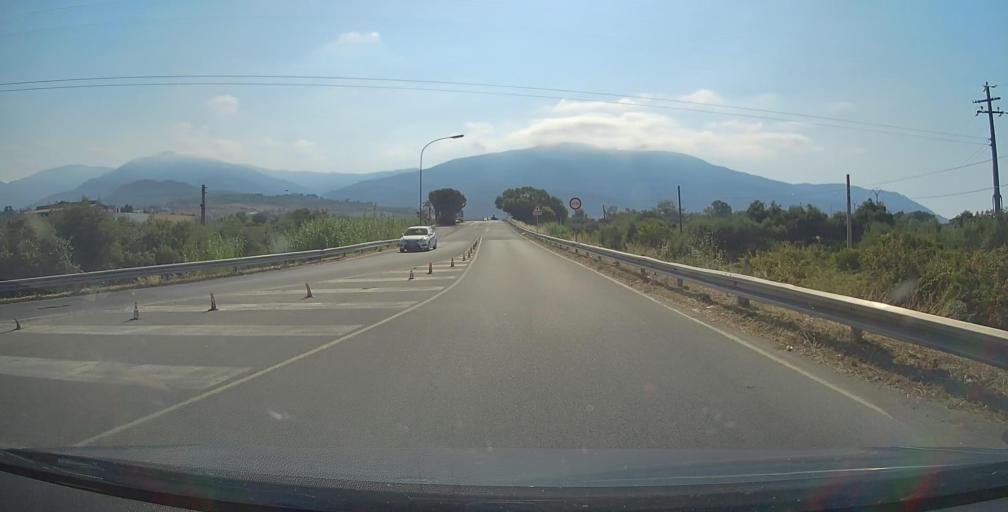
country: IT
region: Sicily
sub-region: Messina
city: Patti
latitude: 38.1460
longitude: 14.9985
